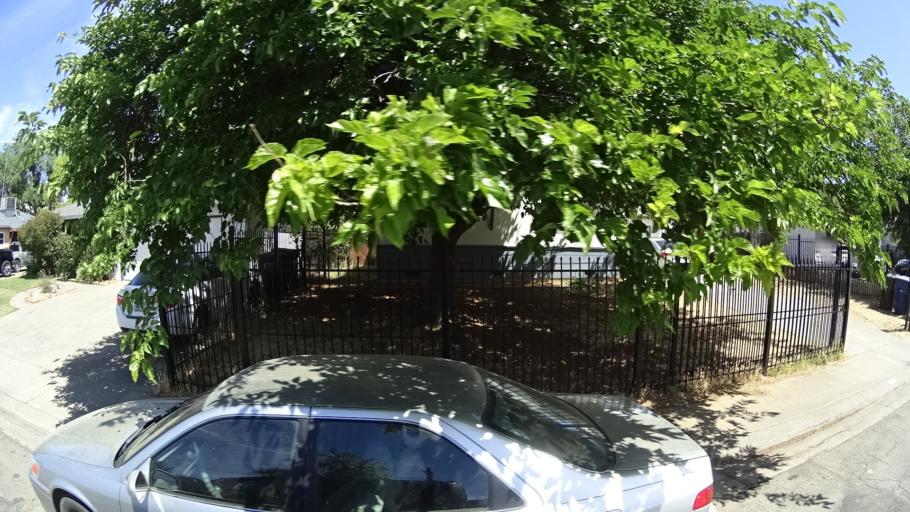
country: US
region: California
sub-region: Sacramento County
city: Florin
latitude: 38.5211
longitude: -121.4242
